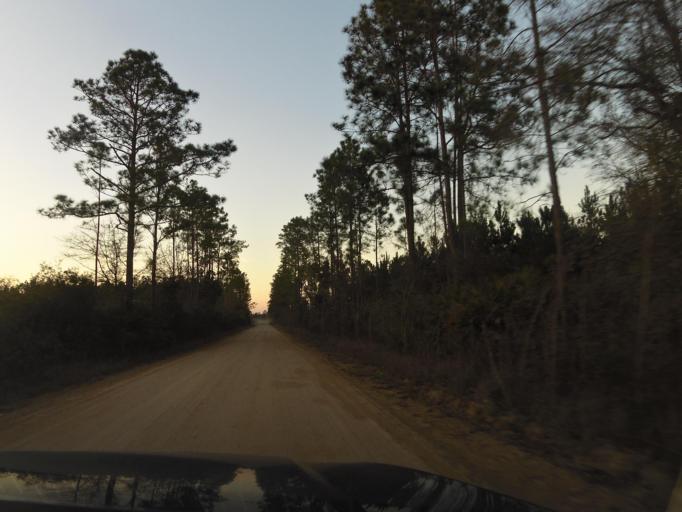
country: US
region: Florida
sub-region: Clay County
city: Asbury Lake
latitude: 29.9571
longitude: -81.7900
